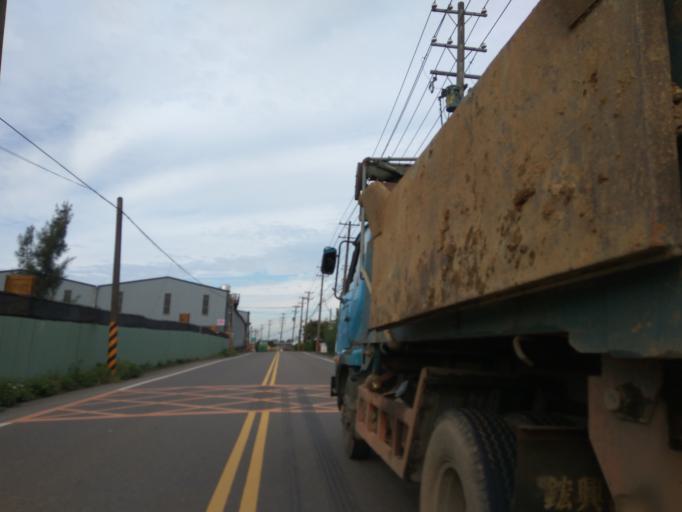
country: TW
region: Taiwan
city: Daxi
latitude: 24.9446
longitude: 121.1502
